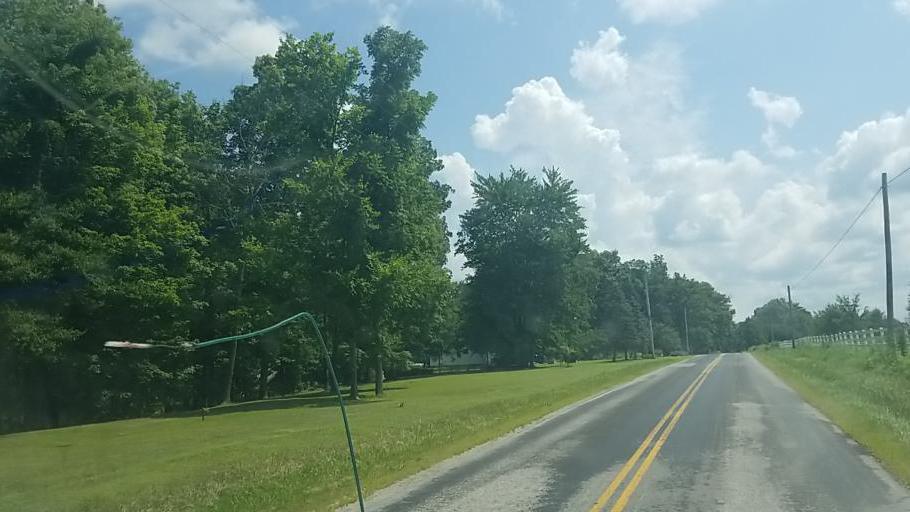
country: US
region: Ohio
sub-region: Wayne County
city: West Salem
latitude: 41.0398
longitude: -82.1346
